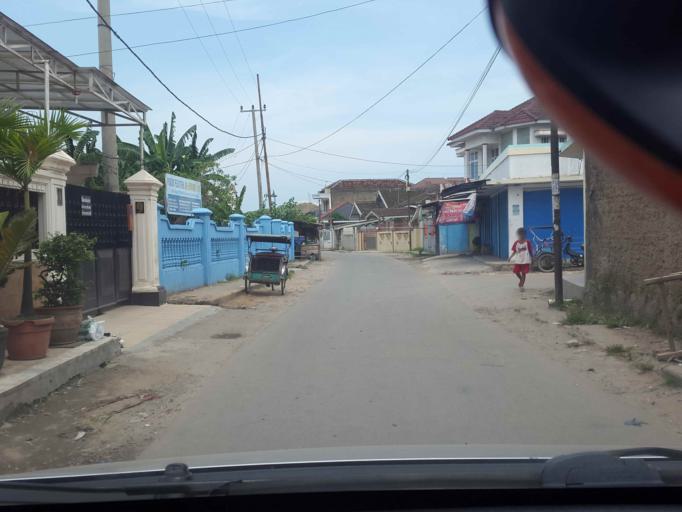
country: ID
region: Lampung
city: Bandarlampung
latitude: -5.4548
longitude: 105.2573
